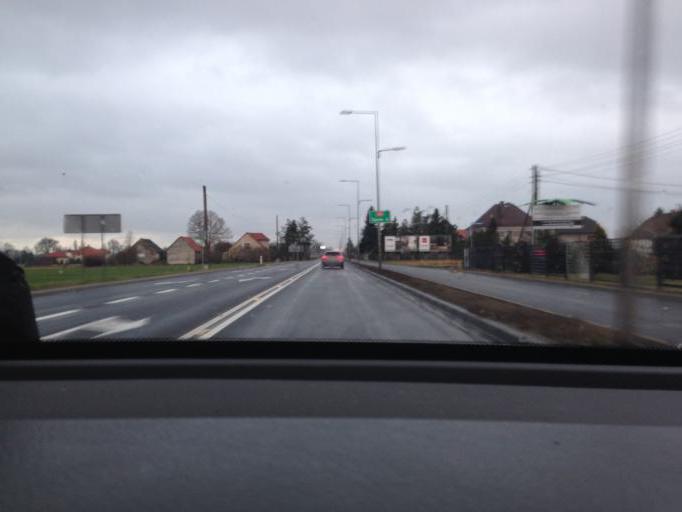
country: PL
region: Opole Voivodeship
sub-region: Powiat opolski
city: Wegry
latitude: 50.7186
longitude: 18.0013
